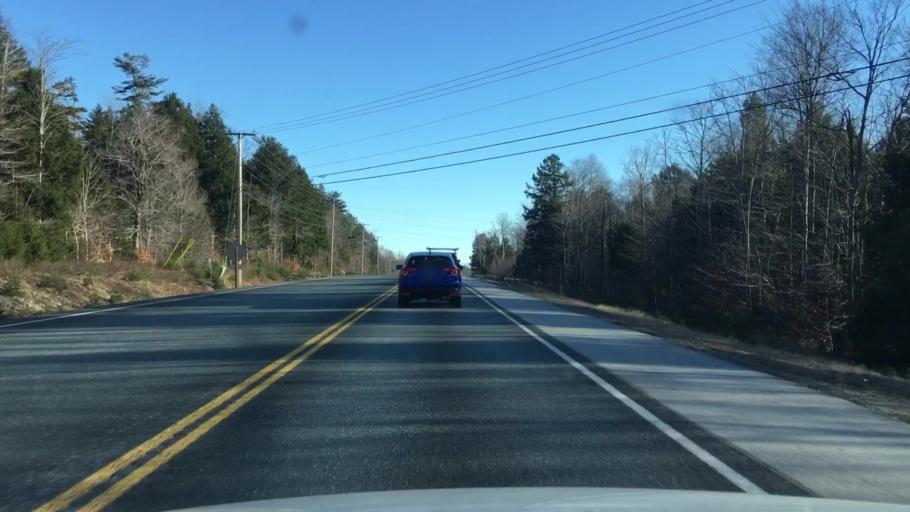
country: US
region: Maine
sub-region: Hancock County
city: Dedham
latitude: 44.6687
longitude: -68.5734
